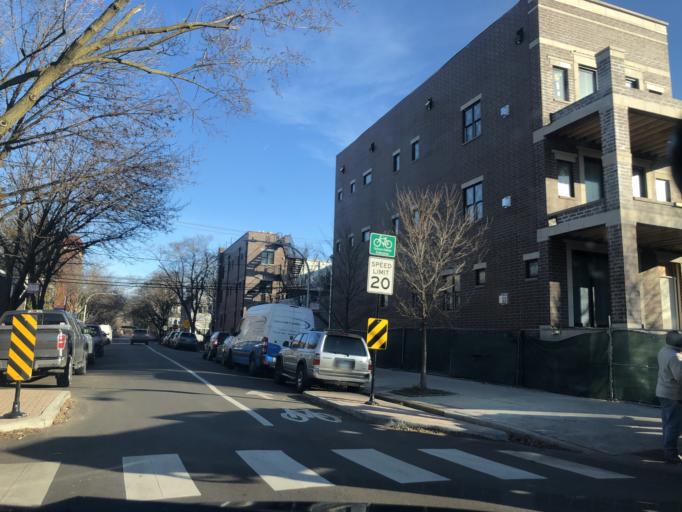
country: US
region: Illinois
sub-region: Cook County
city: Chicago
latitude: 41.9418
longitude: -87.6590
